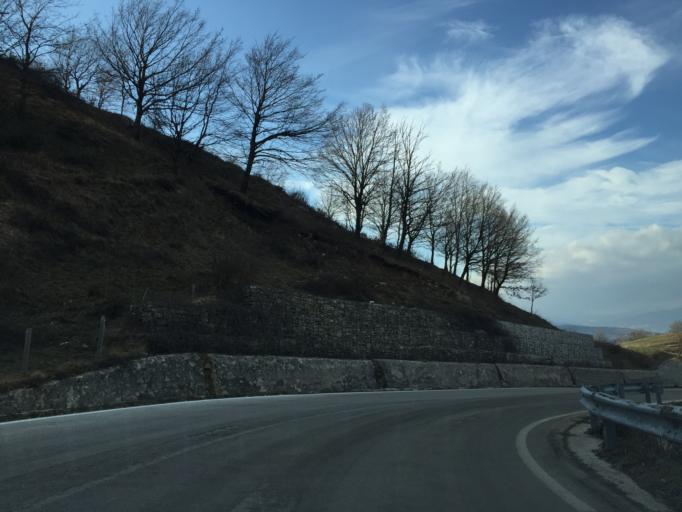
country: IT
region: Molise
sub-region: Provincia di Campobasso
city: San Massimo
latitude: 41.4783
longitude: 14.4076
